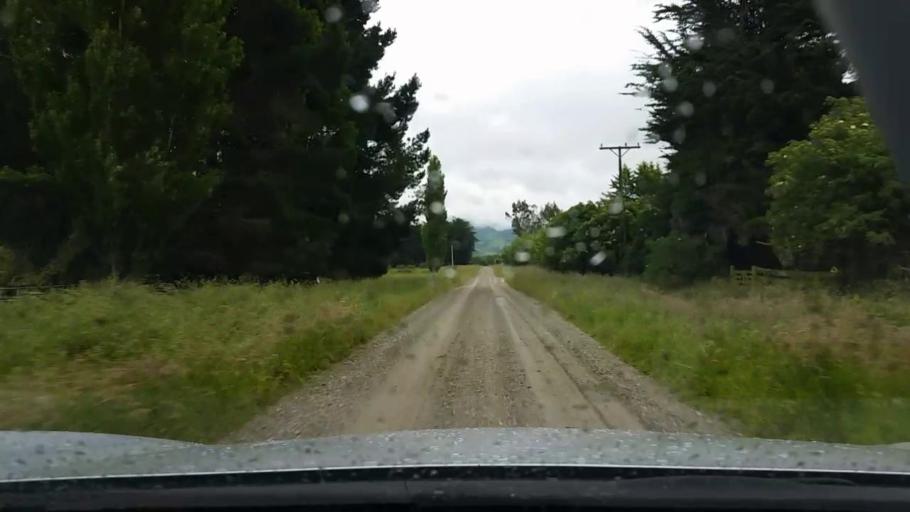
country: NZ
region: Southland
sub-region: Gore District
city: Gore
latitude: -46.0722
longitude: 168.9603
